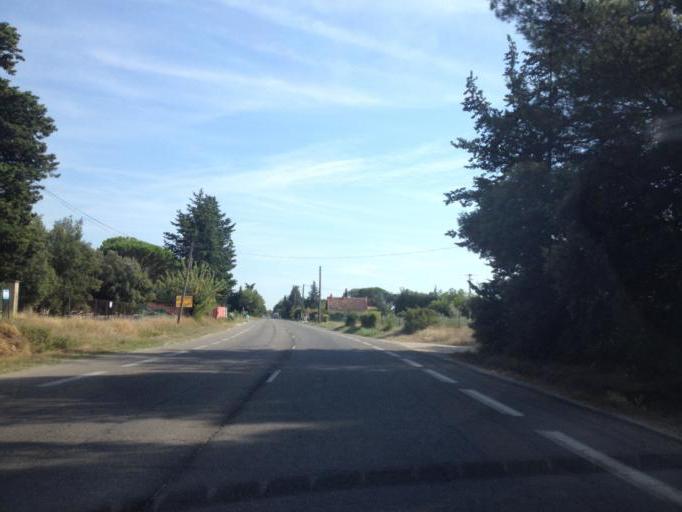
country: FR
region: Provence-Alpes-Cote d'Azur
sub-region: Departement du Vaucluse
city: Carpentras
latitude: 44.0760
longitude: 5.0408
